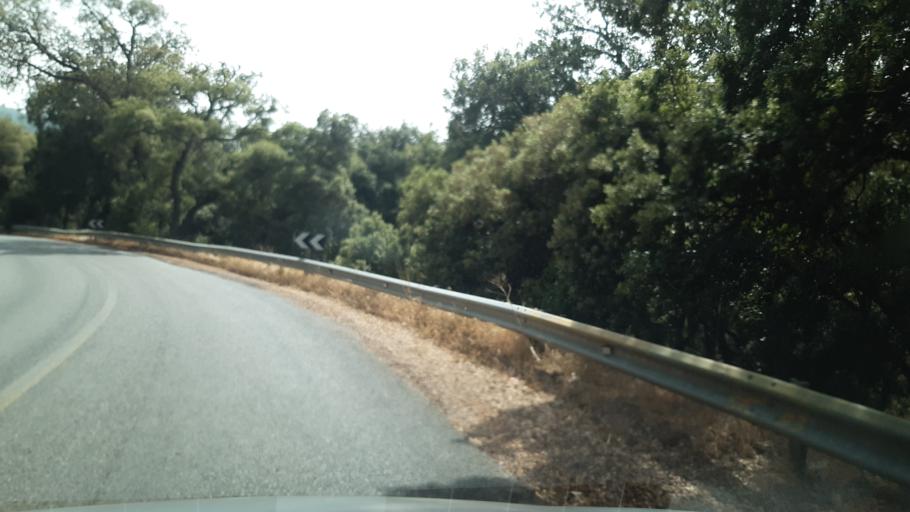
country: MA
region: Meknes-Tafilalet
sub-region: Ifrane
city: Azrou
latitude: 33.4339
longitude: -5.1867
